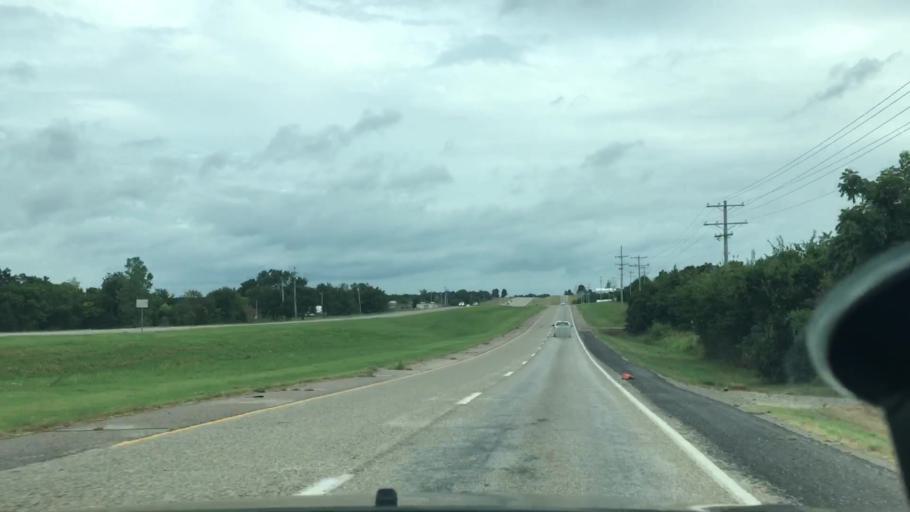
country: US
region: Oklahoma
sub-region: Seminole County
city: Seminole
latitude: 35.2837
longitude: -96.6712
